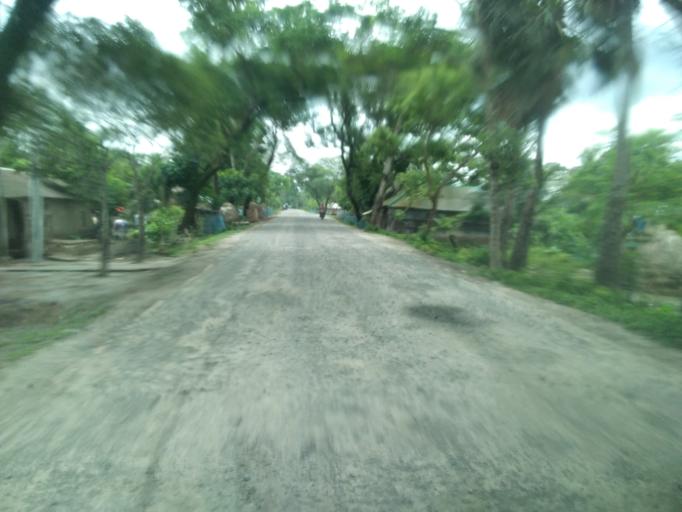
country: IN
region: West Bengal
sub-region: North 24 Parganas
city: Gosaba
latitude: 22.2679
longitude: 89.1638
